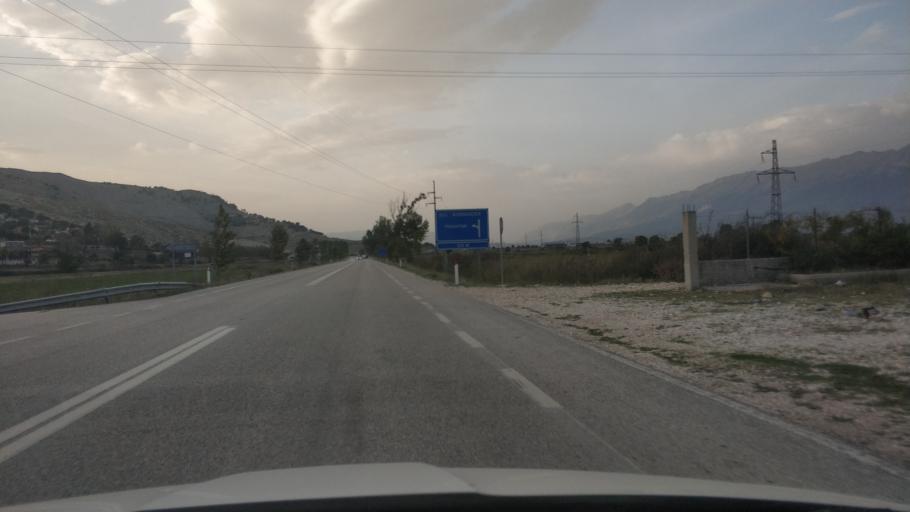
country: AL
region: Gjirokaster
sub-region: Rrethi i Gjirokastres
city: Libohove
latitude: 39.9627
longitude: 20.2436
